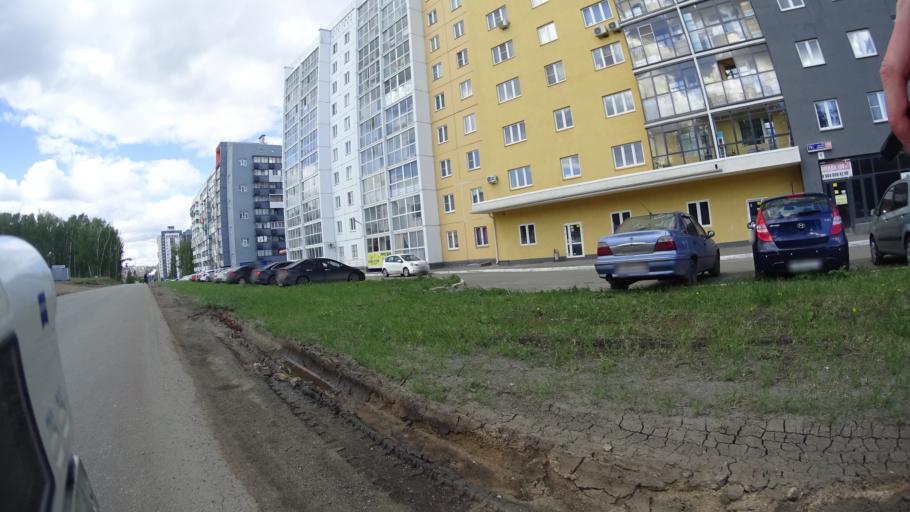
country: RU
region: Chelyabinsk
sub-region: Gorod Chelyabinsk
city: Chelyabinsk
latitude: 55.1602
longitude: 61.2857
